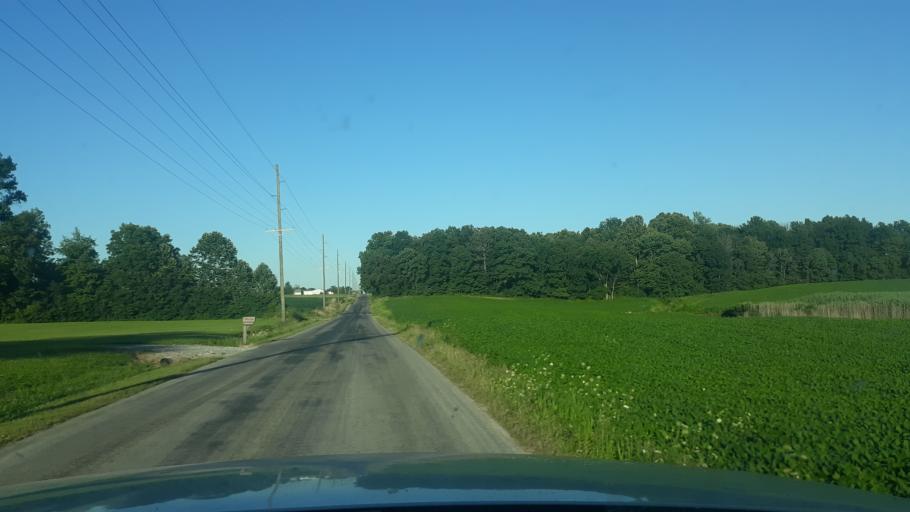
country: US
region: Illinois
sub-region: Saline County
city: Harrisburg
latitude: 37.8631
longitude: -88.5654
